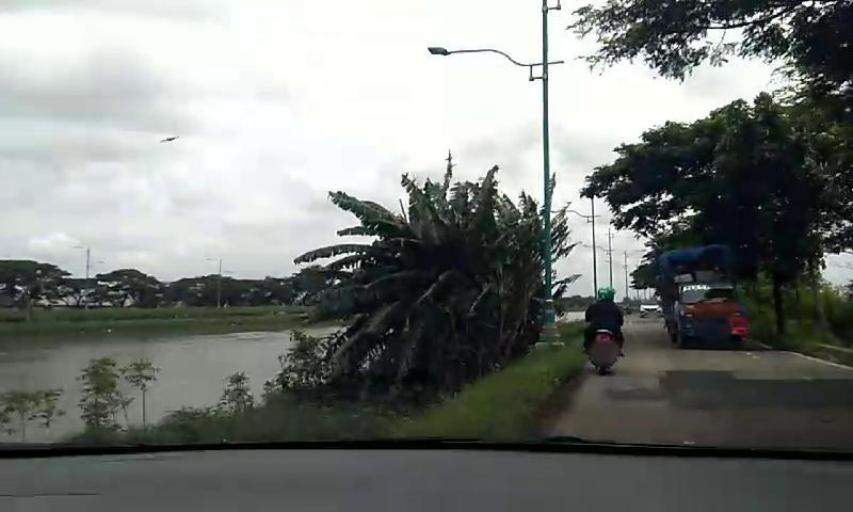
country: ID
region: West Java
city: Bekasi
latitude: -6.1259
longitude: 106.9692
